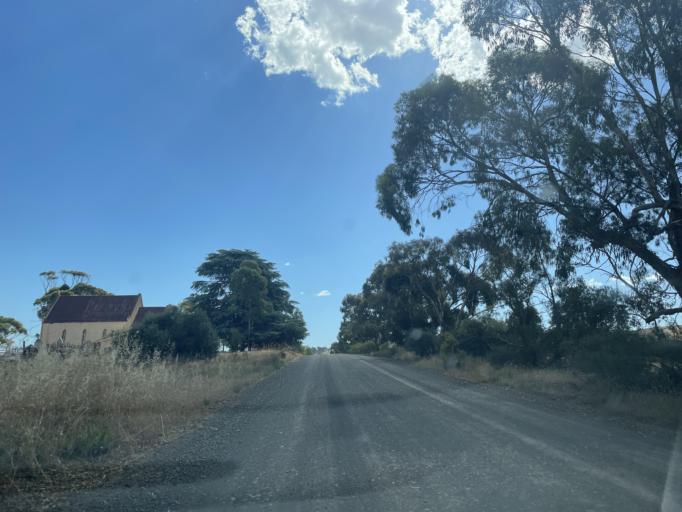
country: AU
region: South Australia
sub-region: Clare and Gilbert Valleys
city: Clare
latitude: -33.9121
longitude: 138.7198
